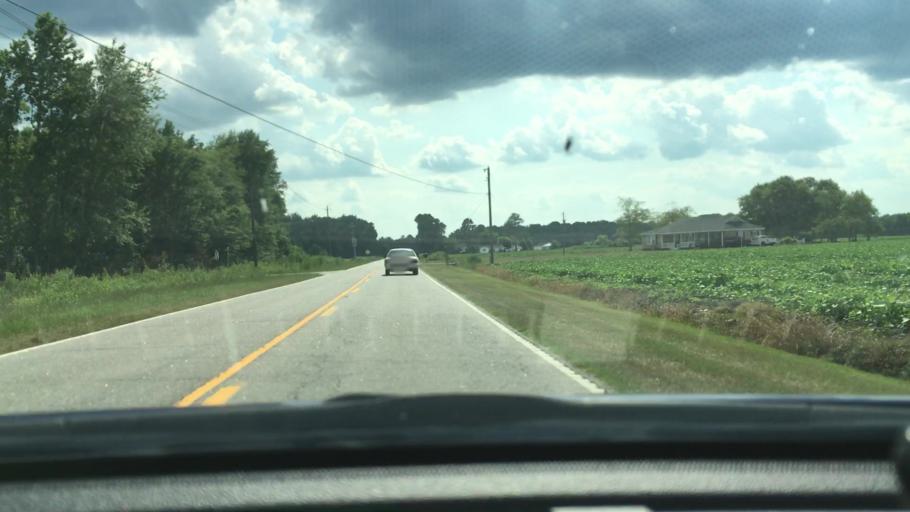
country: US
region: South Carolina
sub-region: Florence County
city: Timmonsville
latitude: 34.1616
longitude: -80.0723
